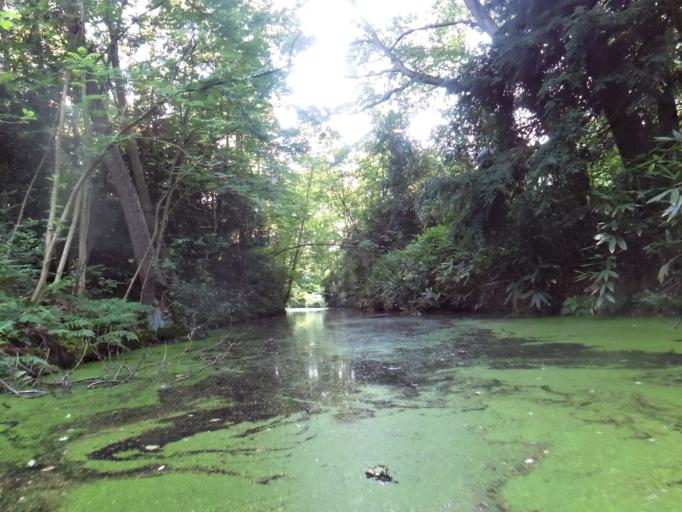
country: NL
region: South Holland
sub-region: Gemeente Wassenaar
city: Wassenaar
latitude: 52.1350
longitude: 4.3856
